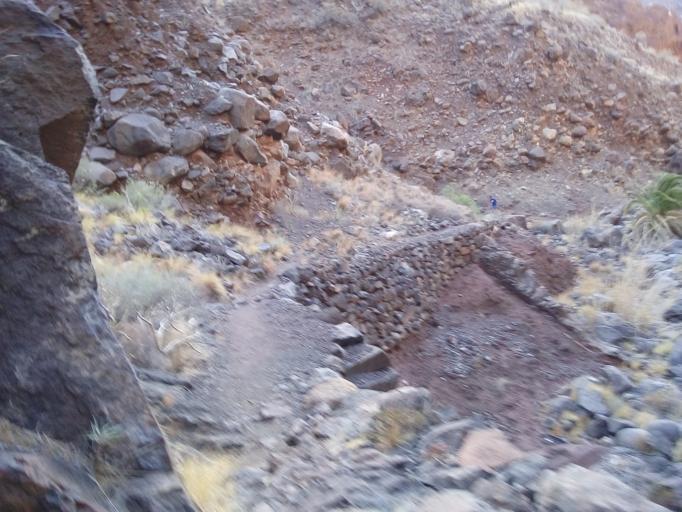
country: ES
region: Canary Islands
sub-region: Provincia de Santa Cruz de Tenerife
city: Alajero
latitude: 28.0844
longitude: -17.3213
